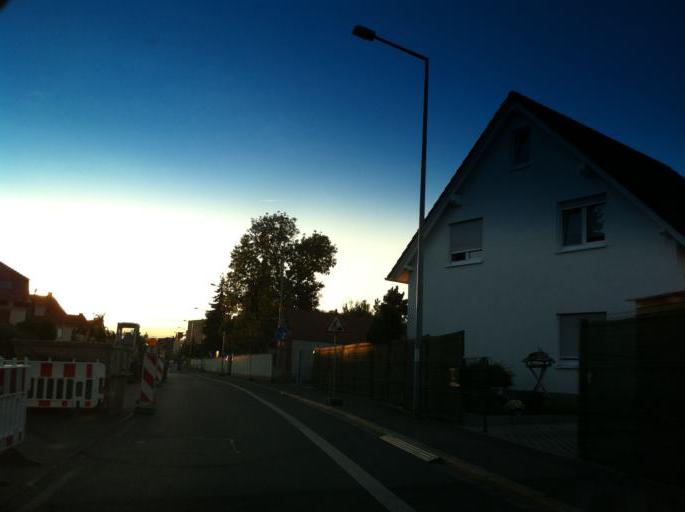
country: DE
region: Saxony
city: Markkleeberg
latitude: 51.2986
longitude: 12.3260
